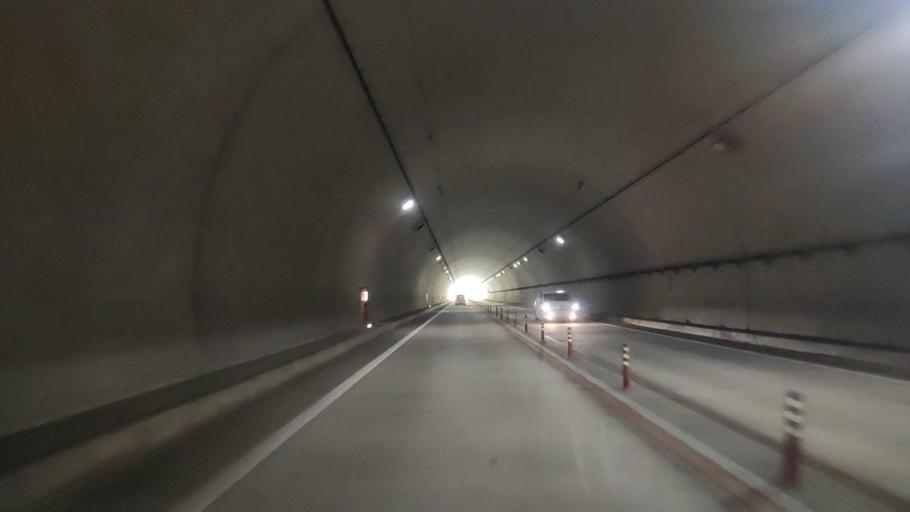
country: JP
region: Wakayama
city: Shingu
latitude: 33.6236
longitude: 135.9196
